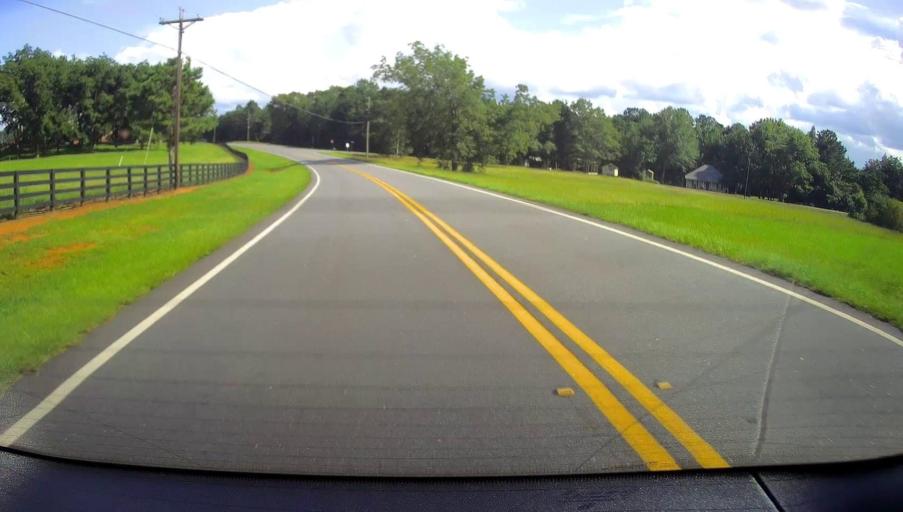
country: US
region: Georgia
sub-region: Upson County
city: Hannahs Mill
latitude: 32.9028
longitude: -84.4222
